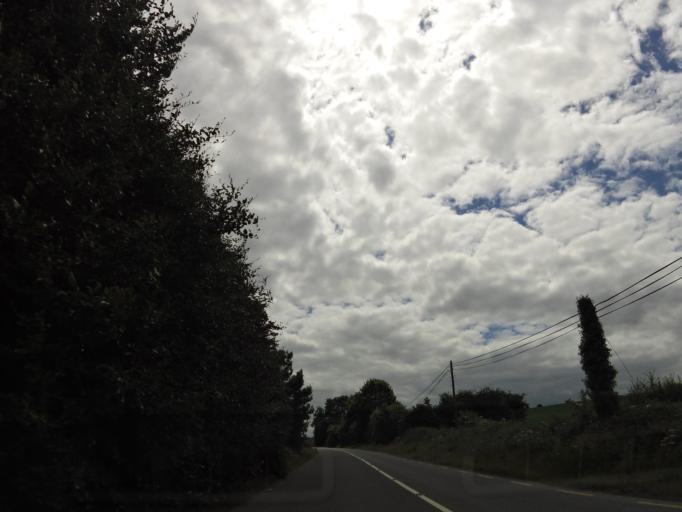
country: IE
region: Munster
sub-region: North Tipperary
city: Templemore
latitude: 52.7708
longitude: -8.0259
